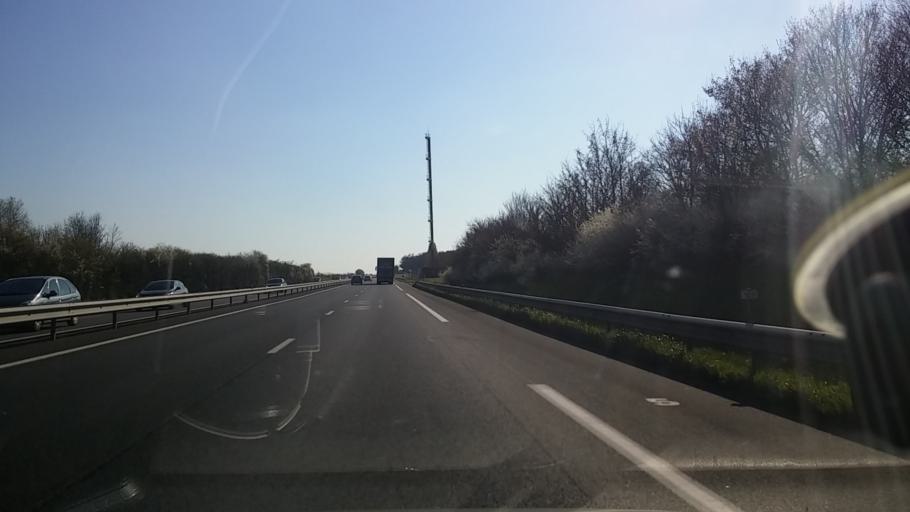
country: FR
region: Centre
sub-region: Departement du Cher
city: Massay
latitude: 47.1581
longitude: 1.9828
